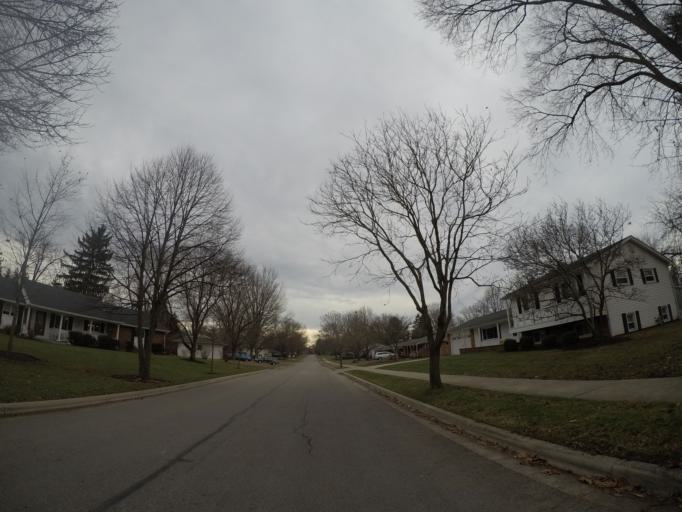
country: US
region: Ohio
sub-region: Franklin County
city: Upper Arlington
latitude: 40.0317
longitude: -83.0769
